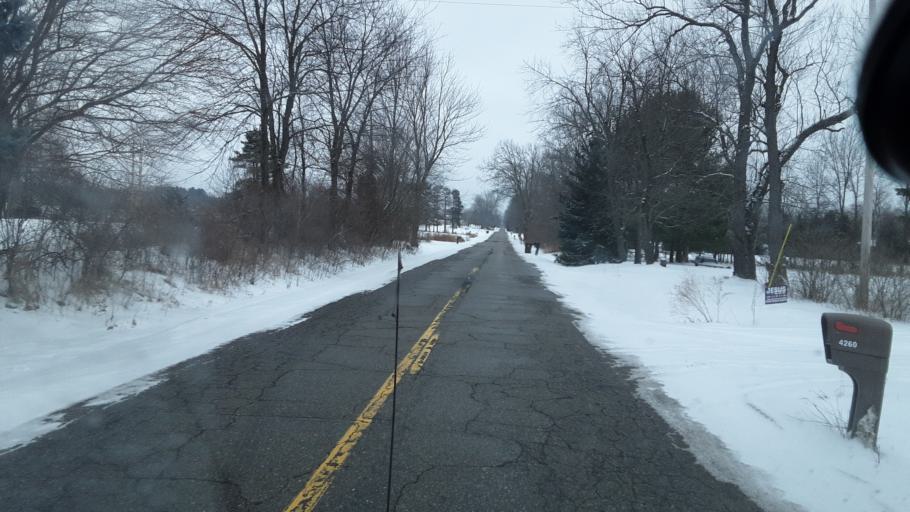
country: US
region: Michigan
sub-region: Ingham County
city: Leslie
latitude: 42.4574
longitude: -84.3941
